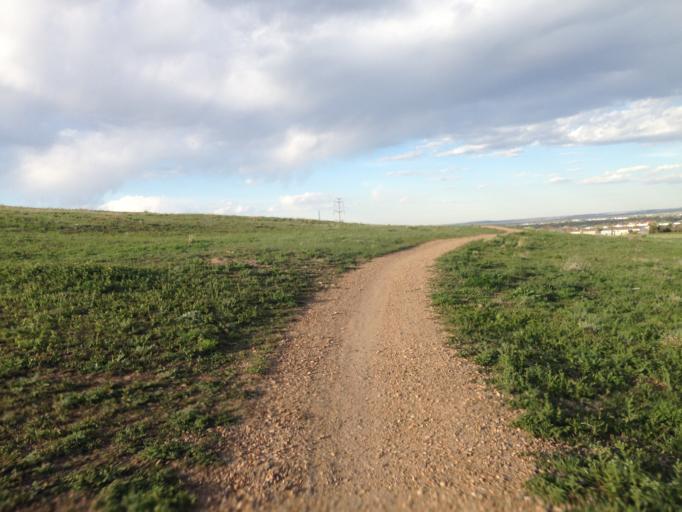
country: US
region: Colorado
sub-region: Boulder County
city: Superior
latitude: 39.9542
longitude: -105.1854
